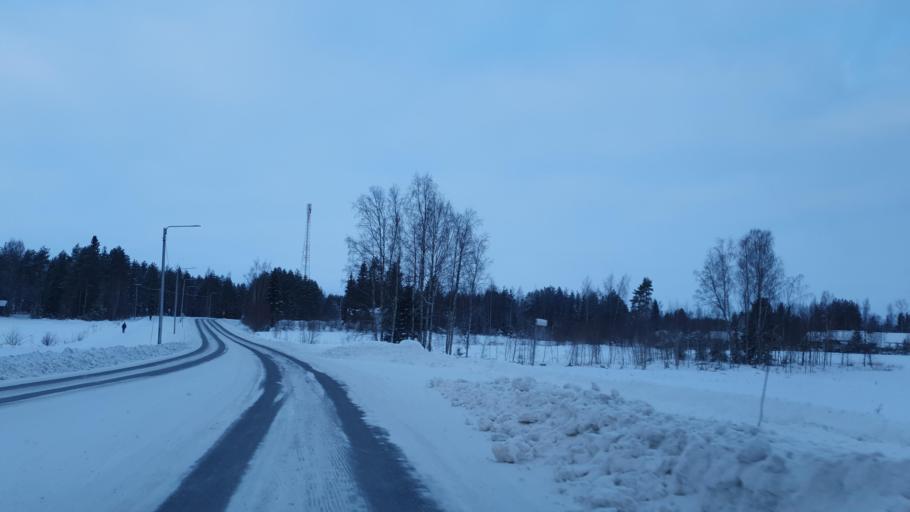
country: FI
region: Northern Ostrobothnia
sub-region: Oulu
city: Haukipudas
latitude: 65.2075
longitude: 25.3295
